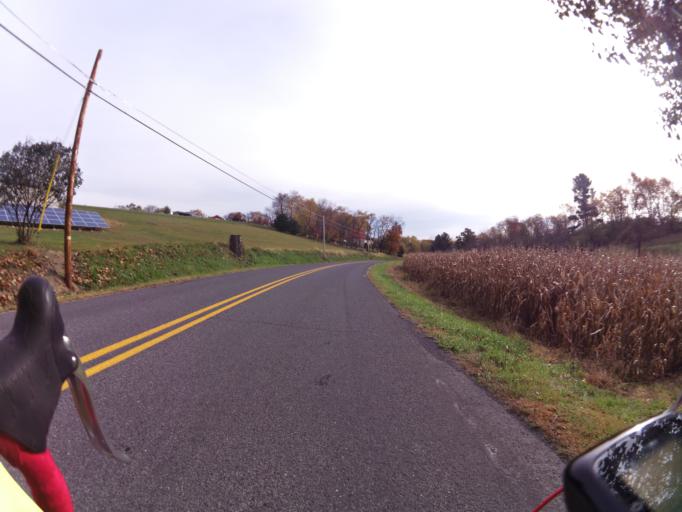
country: US
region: Pennsylvania
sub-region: Union County
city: New Columbia
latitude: 41.0455
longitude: -76.8966
